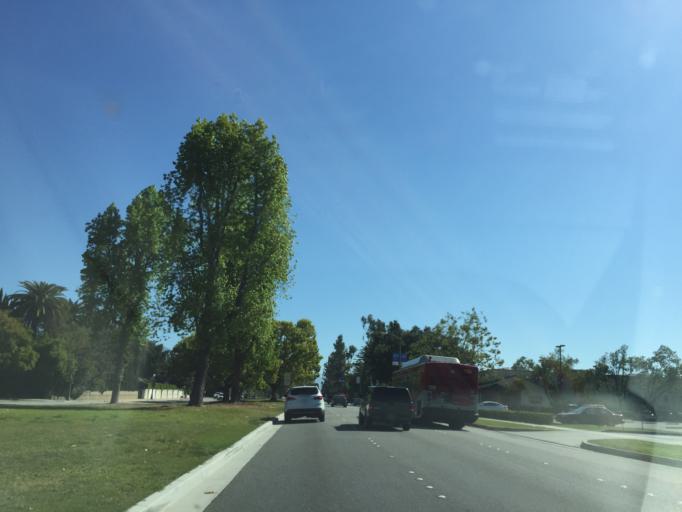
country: US
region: California
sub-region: Los Angeles County
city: San Marino
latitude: 34.1187
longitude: -118.1146
